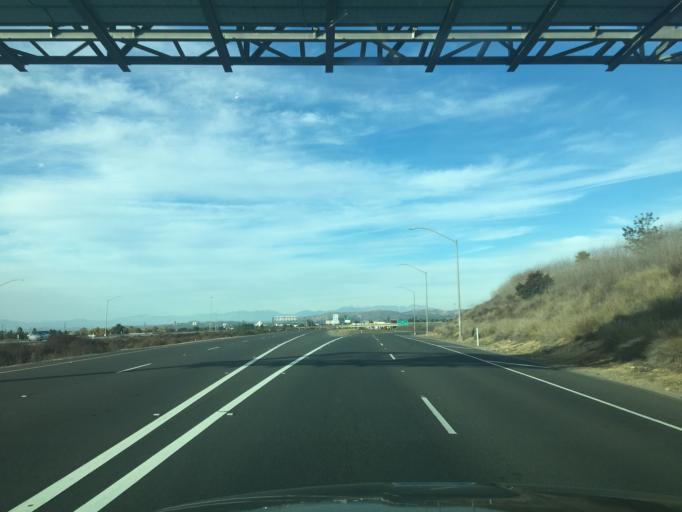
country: US
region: California
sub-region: Orange County
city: Laguna Woods
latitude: 33.6470
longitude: -117.7618
